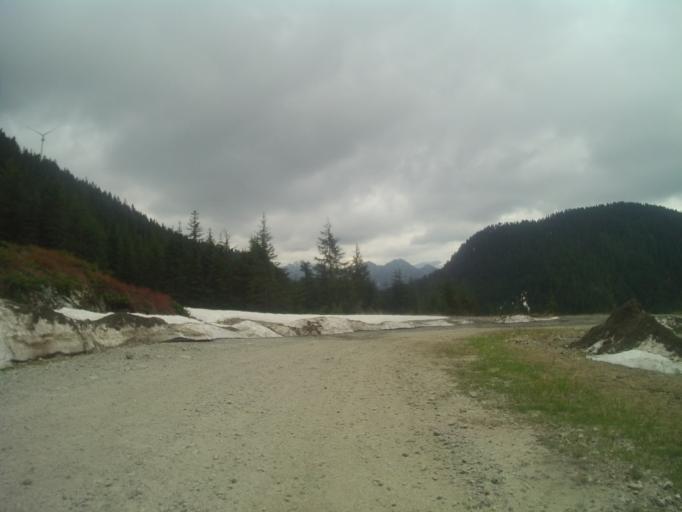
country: CA
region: British Columbia
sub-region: Fraser Valley Regional District
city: North Vancouver
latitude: 49.3807
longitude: -123.0747
